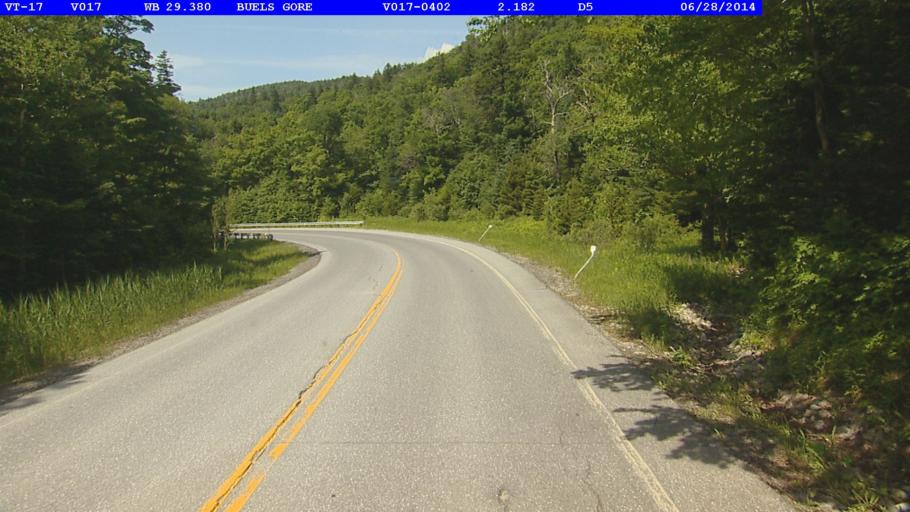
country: US
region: Vermont
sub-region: Addison County
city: Bristol
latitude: 44.2128
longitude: -72.9356
